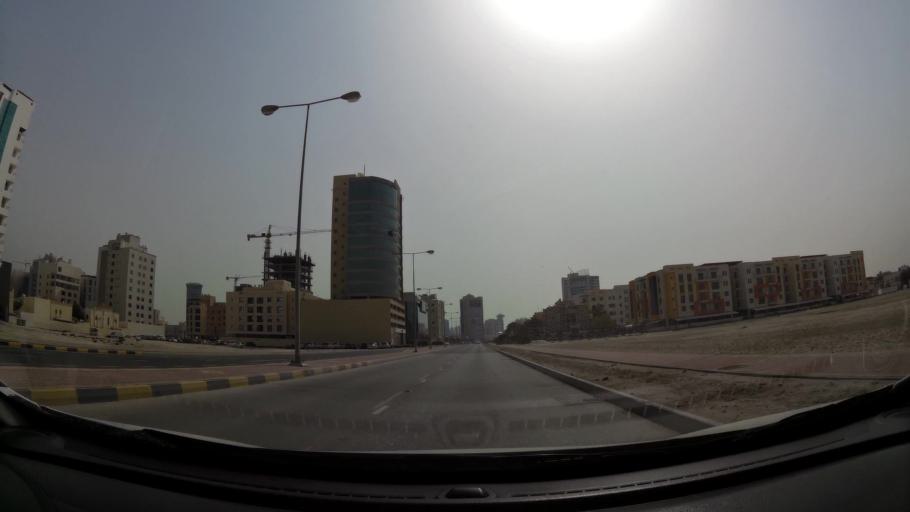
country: BH
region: Manama
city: Jidd Hafs
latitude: 26.2362
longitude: 50.5295
